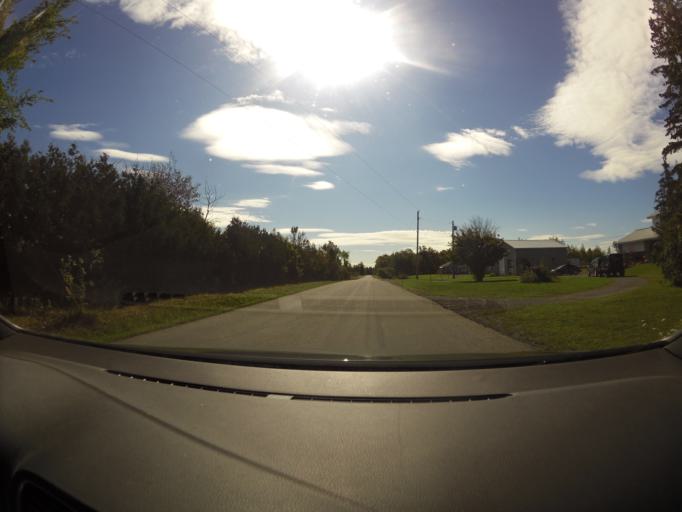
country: CA
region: Ontario
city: Bells Corners
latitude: 45.2692
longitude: -75.9653
